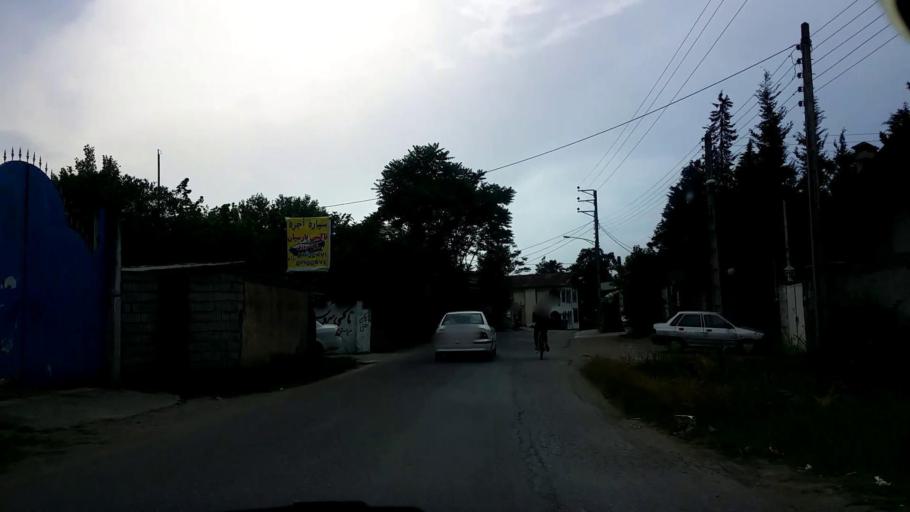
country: IR
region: Mazandaran
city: Chalus
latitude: 36.6854
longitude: 51.4157
